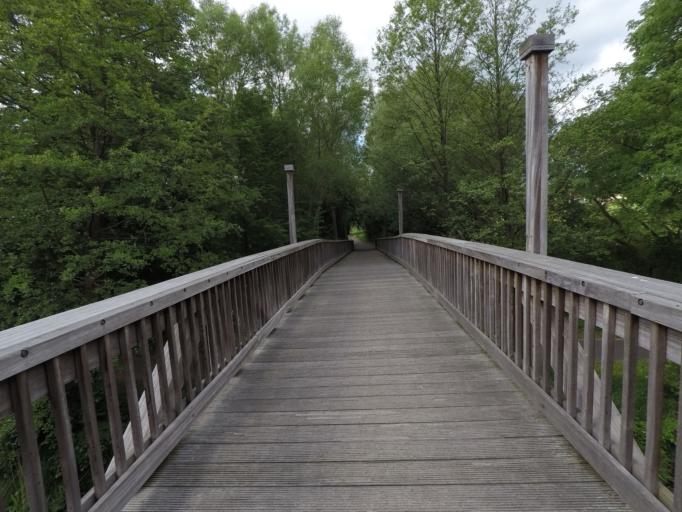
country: DE
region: Brandenburg
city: Melchow
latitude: 52.8455
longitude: 13.6959
